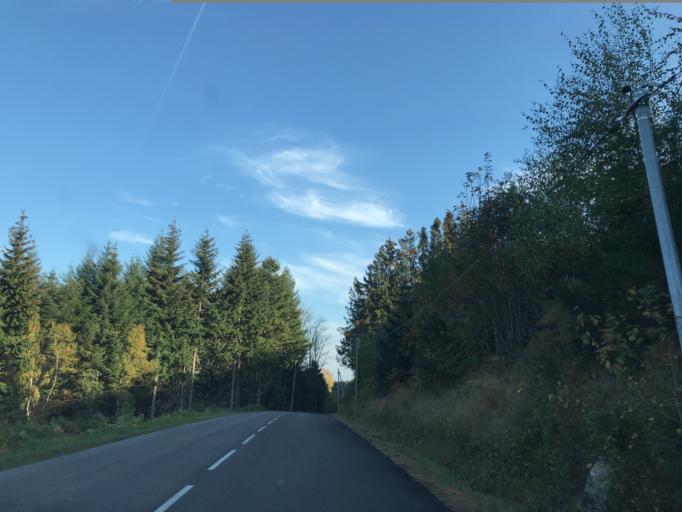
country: FR
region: Rhone-Alpes
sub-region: Departement de la Loire
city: Noiretable
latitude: 45.8072
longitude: 3.7295
